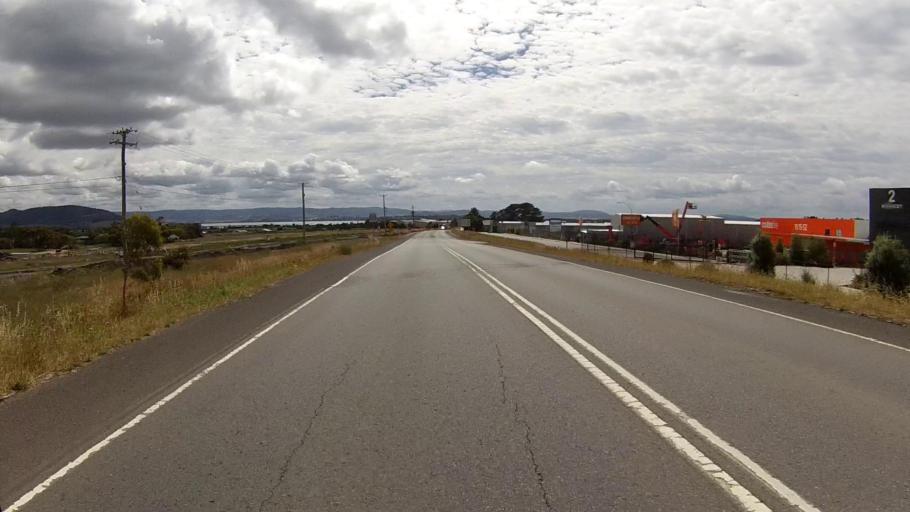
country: AU
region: Tasmania
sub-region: Clarence
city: Cambridge
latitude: -42.8337
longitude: 147.4560
